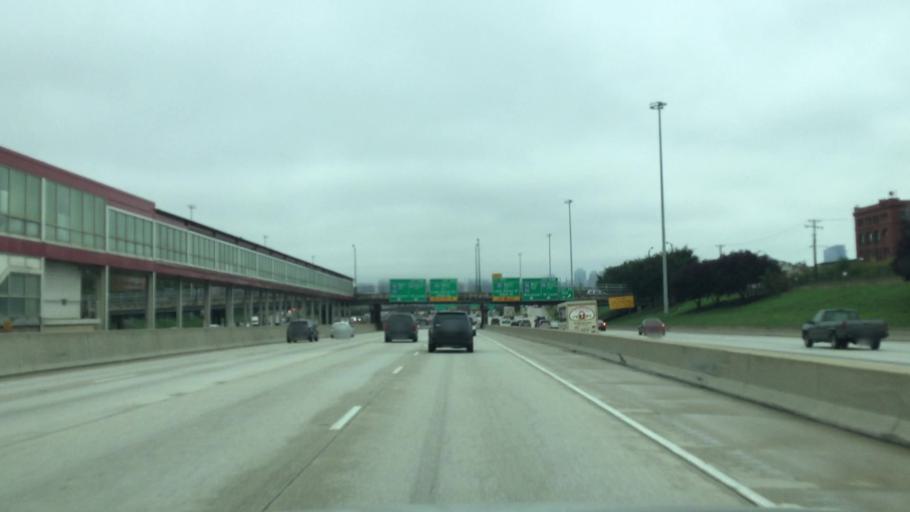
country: US
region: Illinois
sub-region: Cook County
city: Chicago
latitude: 41.8329
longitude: -87.6305
